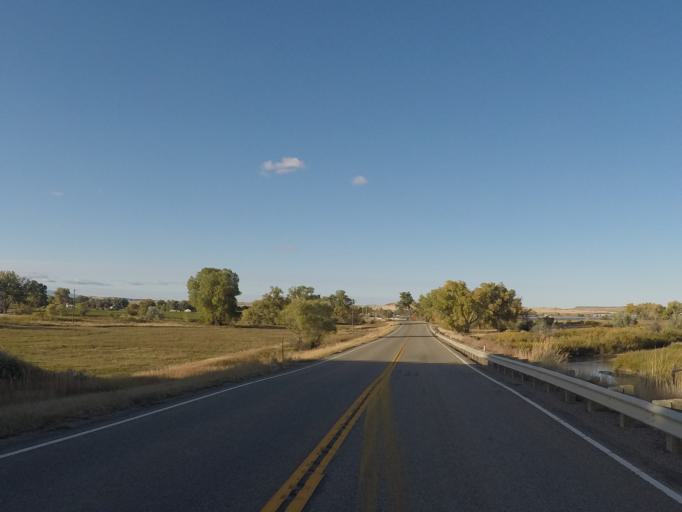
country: US
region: Montana
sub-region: Golden Valley County
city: Ryegate
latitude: 46.2853
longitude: -108.9384
